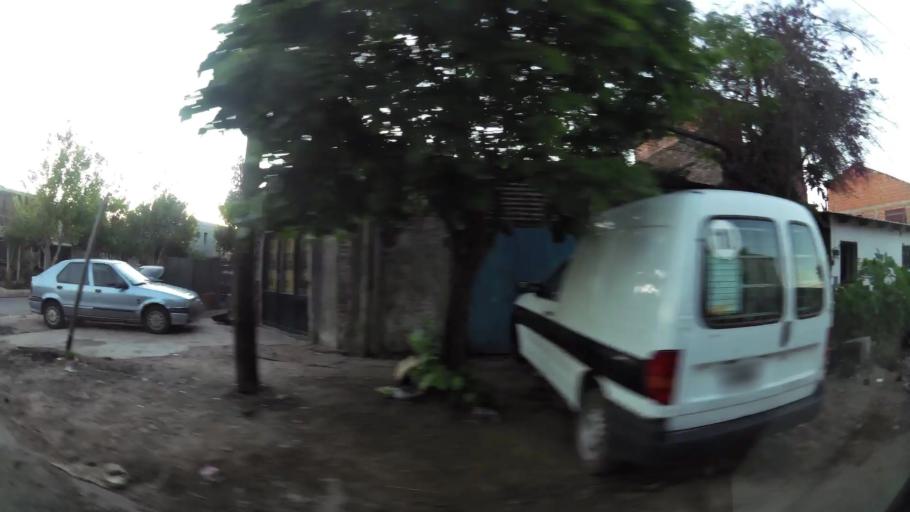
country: AR
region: Santa Fe
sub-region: Departamento de Rosario
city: Rosario
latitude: -32.9692
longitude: -60.6875
